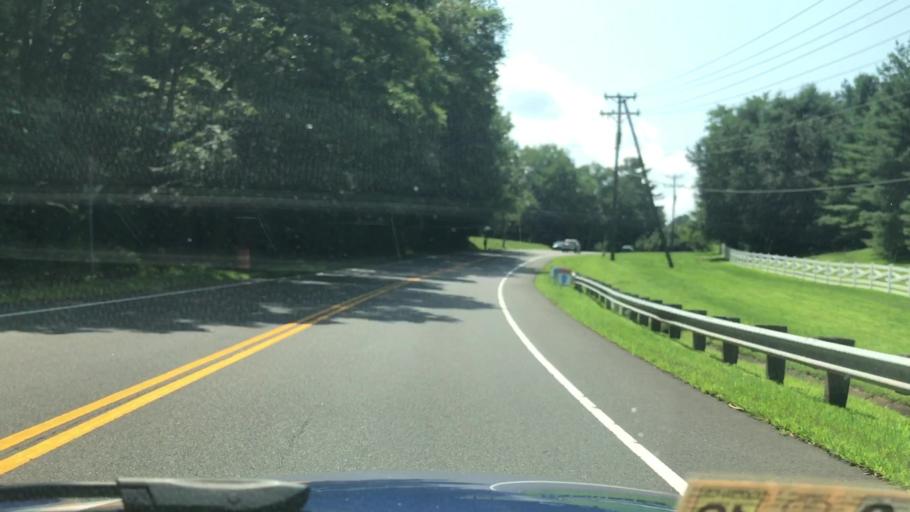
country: US
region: Virginia
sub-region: Fairfax County
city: Wolf Trap
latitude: 38.9181
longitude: -77.3040
